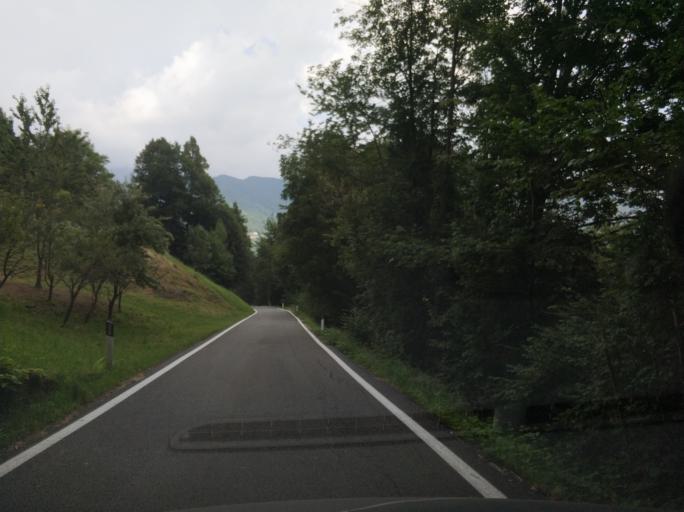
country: IT
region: Piedmont
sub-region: Provincia di Torino
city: Viu
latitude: 45.2248
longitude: 7.3784
